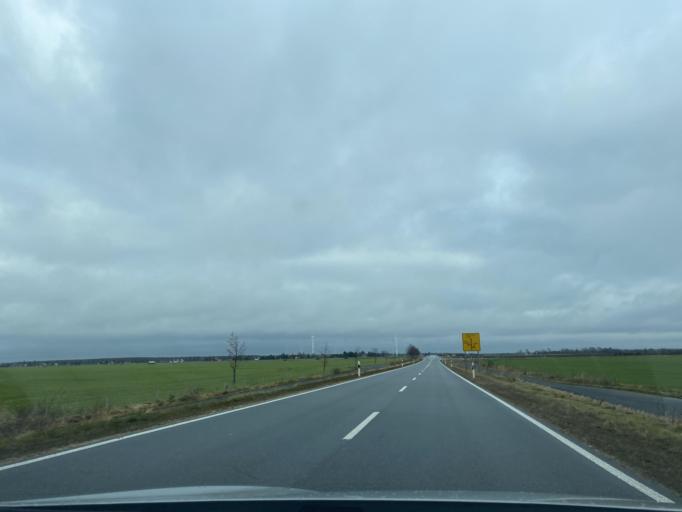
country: PL
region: Lower Silesian Voivodeship
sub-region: Powiat zgorzelecki
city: Piensk
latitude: 51.2313
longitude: 14.9762
